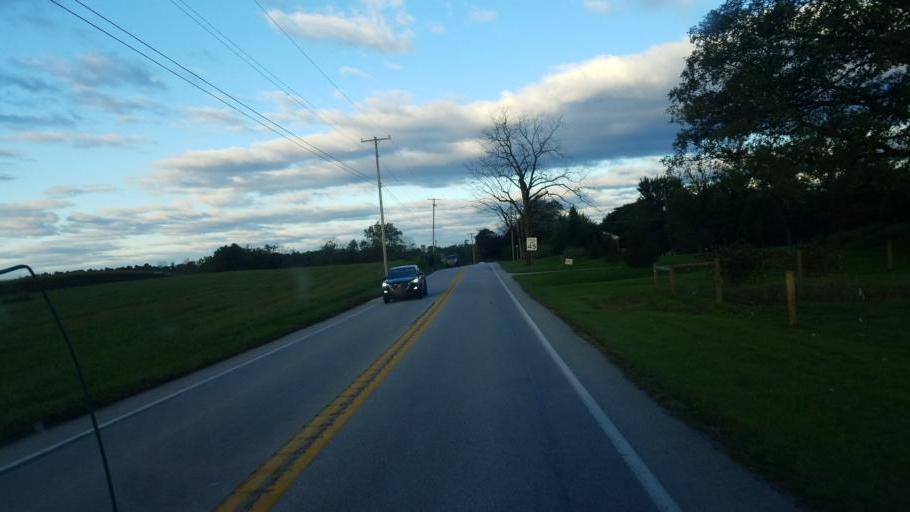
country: US
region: Pennsylvania
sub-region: Adams County
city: East Berlin
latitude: 39.9363
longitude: -76.9271
